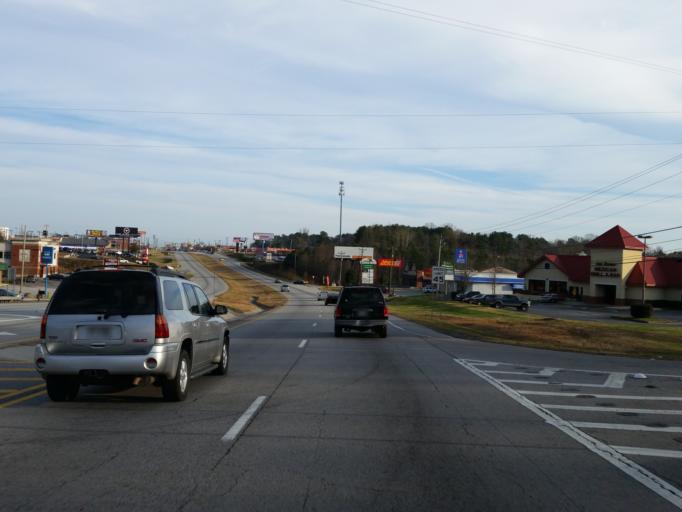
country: US
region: Georgia
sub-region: Paulding County
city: Hiram
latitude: 33.8960
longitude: -84.7661
